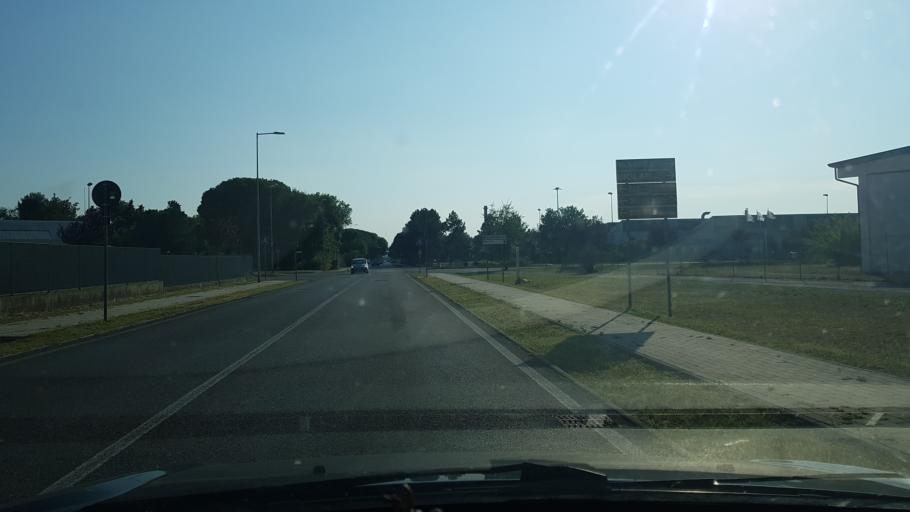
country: IT
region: Friuli Venezia Giulia
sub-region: Provincia di Gorizia
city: Savogna d'Isonzo
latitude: 45.9141
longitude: 13.5922
